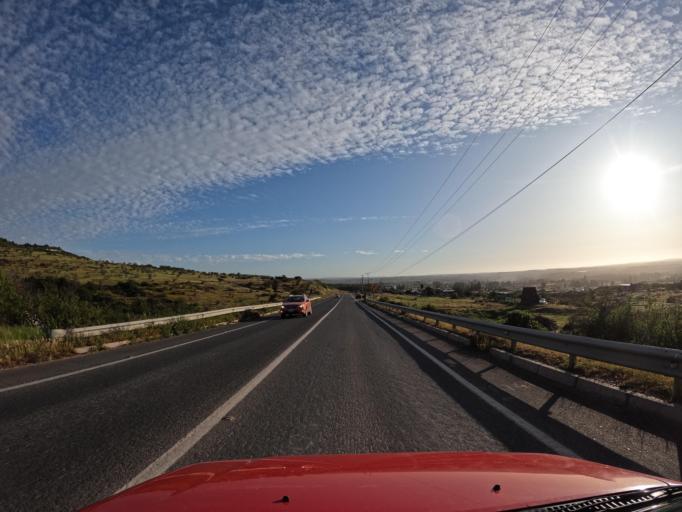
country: CL
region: Valparaiso
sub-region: San Antonio Province
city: San Antonio
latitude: -34.0931
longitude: -71.6858
